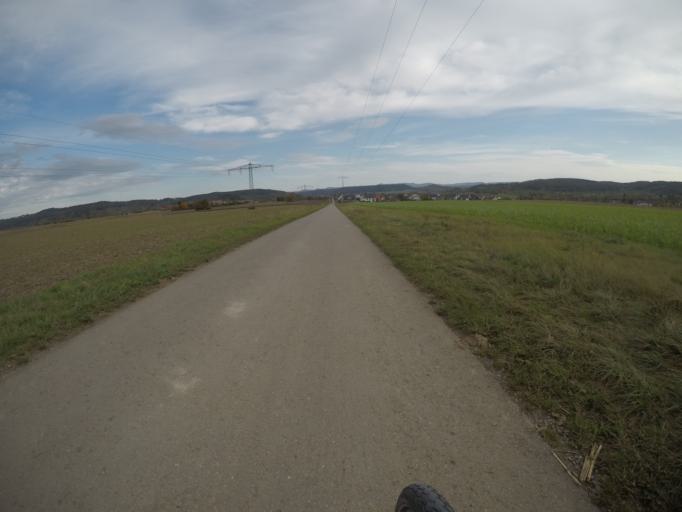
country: DE
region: Baden-Wuerttemberg
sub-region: Tuebingen Region
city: Rottenburg
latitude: 48.5411
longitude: 8.9419
